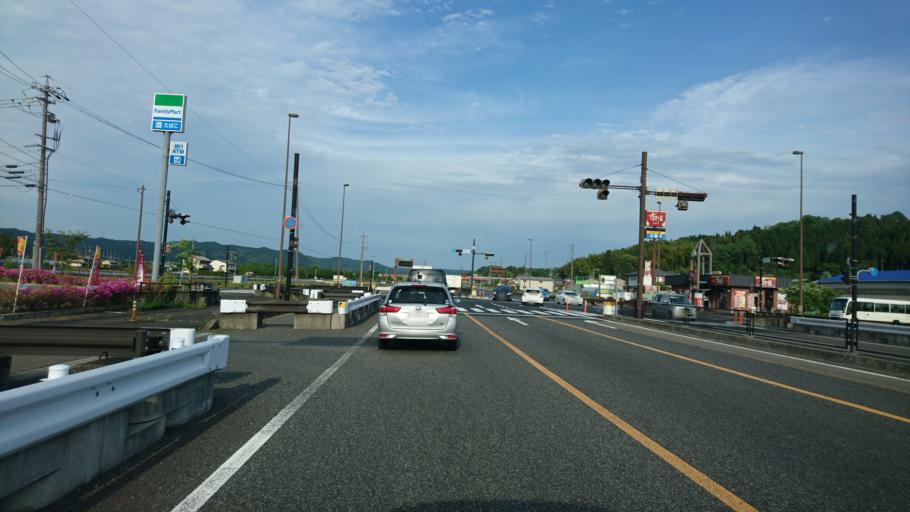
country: JP
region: Gifu
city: Mitake
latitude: 35.4305
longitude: 137.0913
